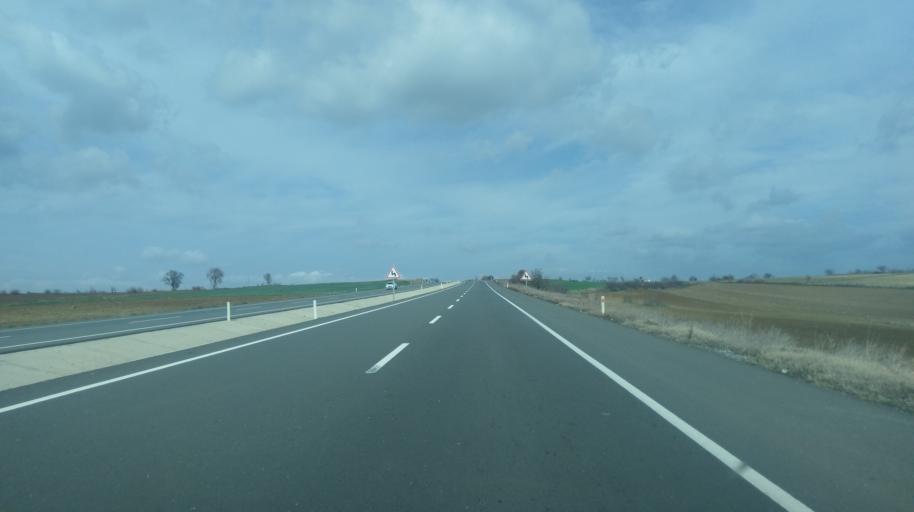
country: TR
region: Edirne
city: Hamidiye
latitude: 41.0556
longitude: 26.6395
